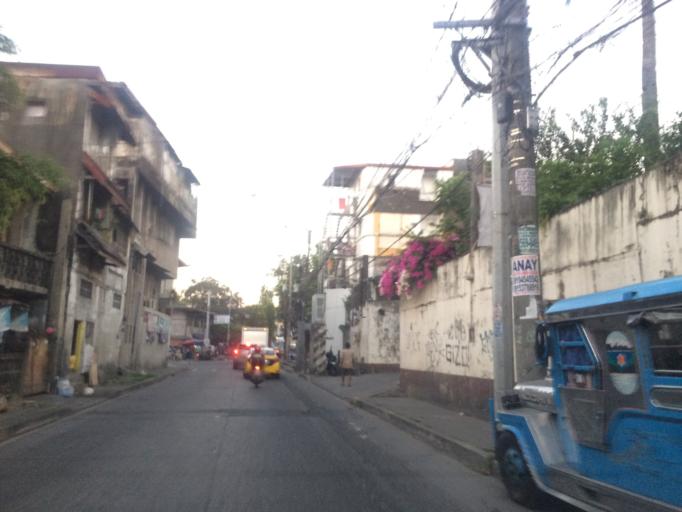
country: PH
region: Calabarzon
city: Del Monte
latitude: 14.6413
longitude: 121.0130
